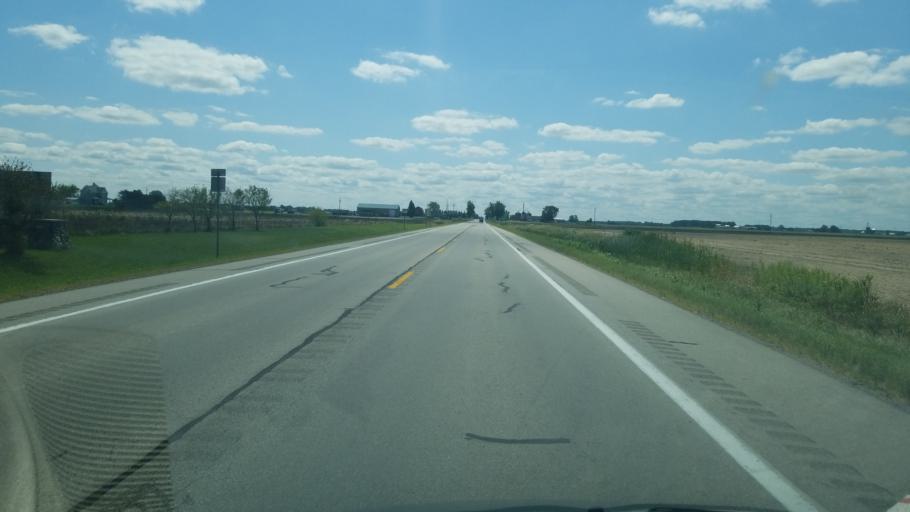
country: US
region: Ohio
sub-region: Fulton County
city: Delta
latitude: 41.7179
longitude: -84.0375
